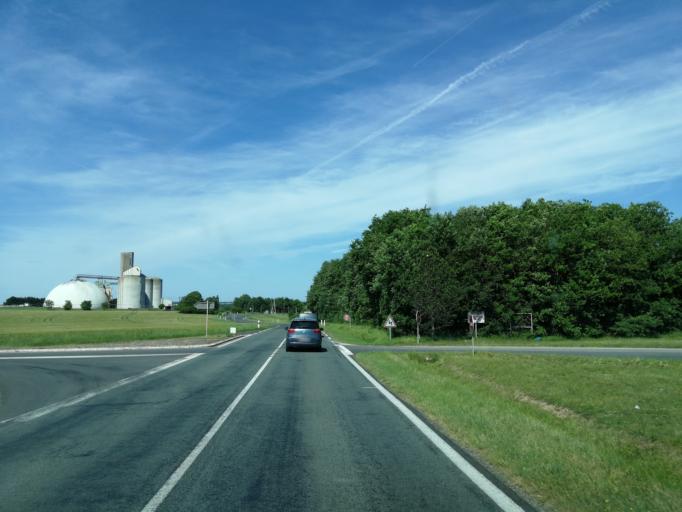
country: FR
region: Poitou-Charentes
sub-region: Departement de la Vienne
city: Loudun
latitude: 47.0630
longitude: 0.1597
